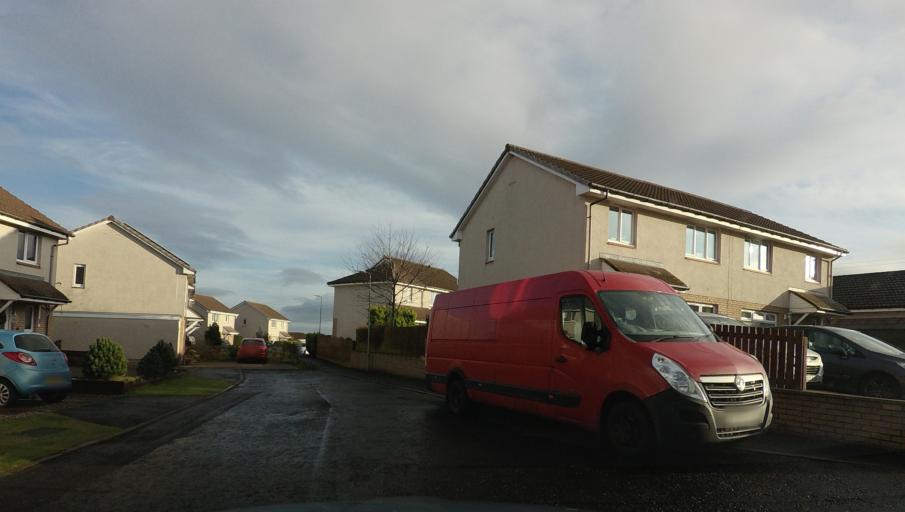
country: GB
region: Scotland
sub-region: West Lothian
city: Kirknewton
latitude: 55.8893
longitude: -3.4297
